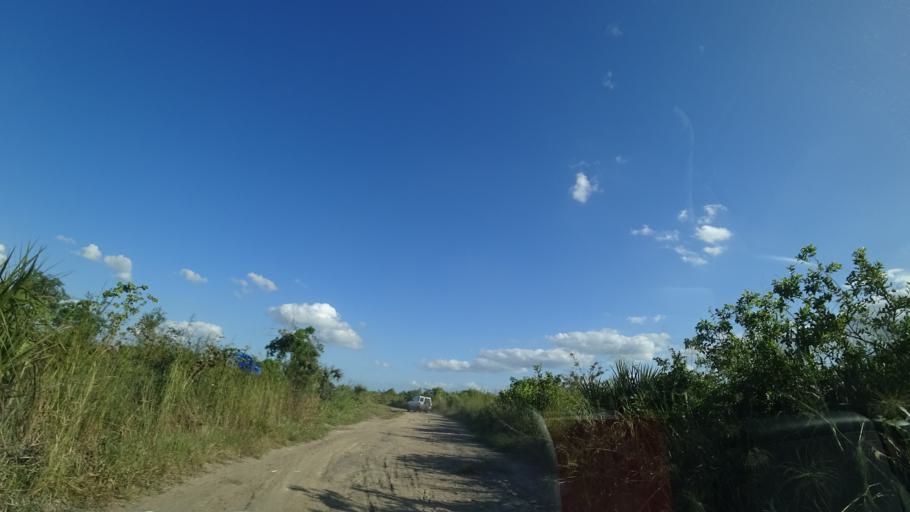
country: MZ
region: Sofala
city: Dondo
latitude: -19.3677
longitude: 34.5911
